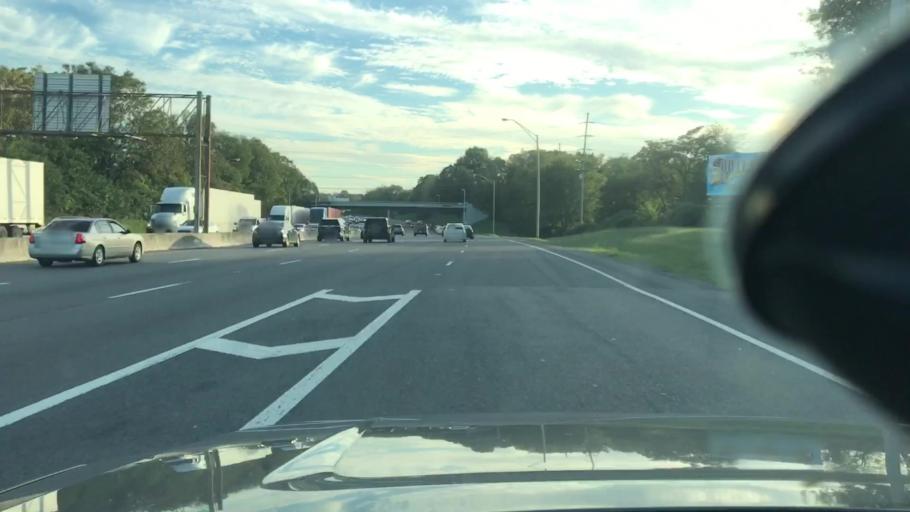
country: US
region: Tennessee
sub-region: Davidson County
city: Nashville
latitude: 36.1827
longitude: -86.7999
